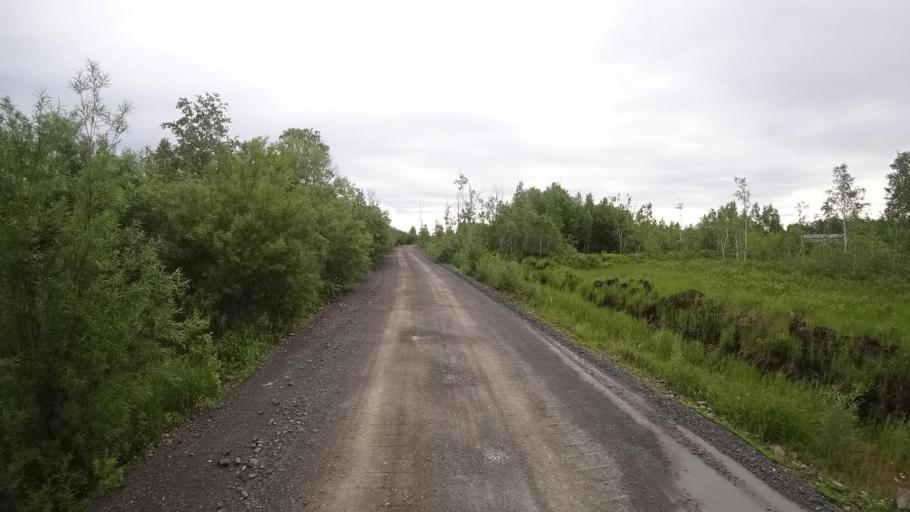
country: RU
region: Khabarovsk Krai
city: Amursk
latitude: 49.8994
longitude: 136.1327
